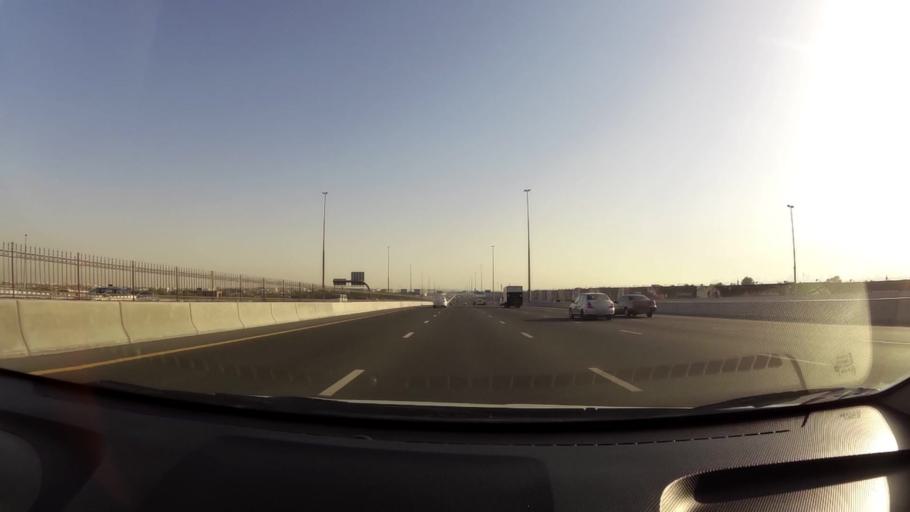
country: AE
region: Ash Shariqah
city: Sharjah
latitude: 25.3327
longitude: 55.4639
